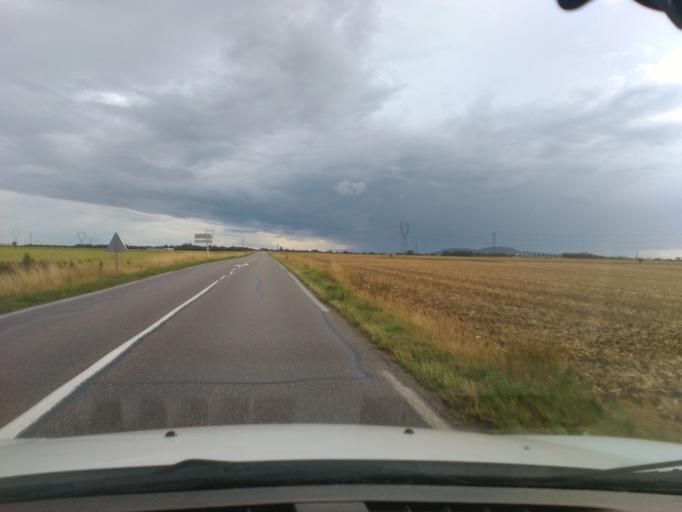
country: FR
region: Lorraine
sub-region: Departement de Meurthe-et-Moselle
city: Pulligny
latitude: 48.4880
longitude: 6.1446
